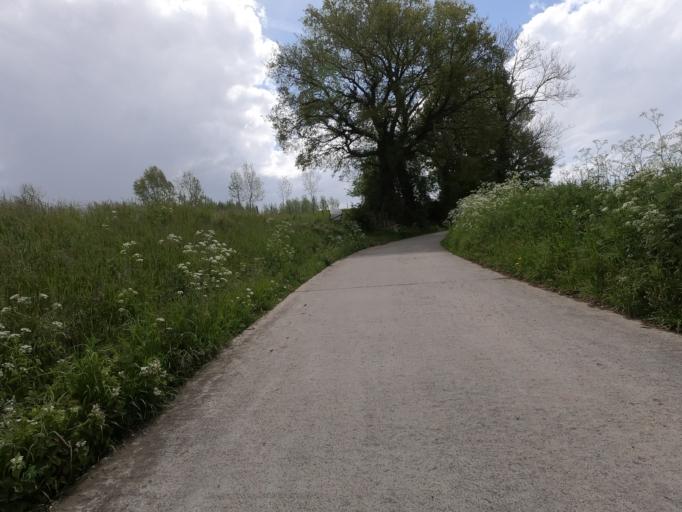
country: BE
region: Flanders
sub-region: Provincie Oost-Vlaanderen
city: Ronse
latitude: 50.7869
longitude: 3.5485
